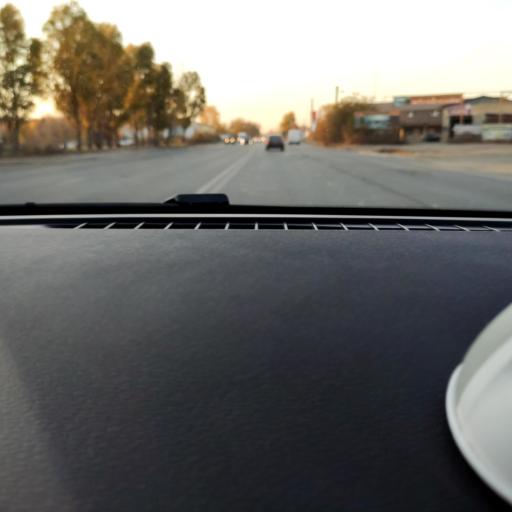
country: RU
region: Samara
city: Petra-Dubrava
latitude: 53.2636
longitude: 50.2872
